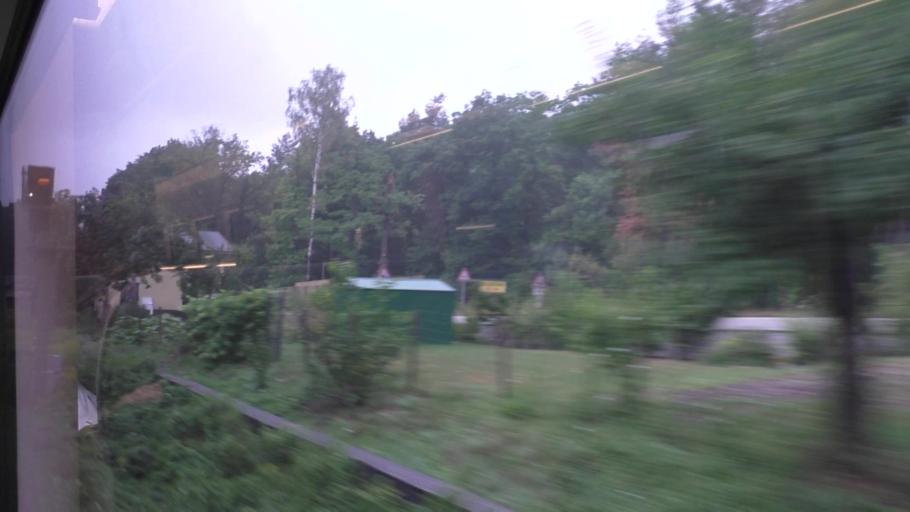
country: DE
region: Saxony
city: Bischofswerda
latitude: 51.1299
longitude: 14.2054
